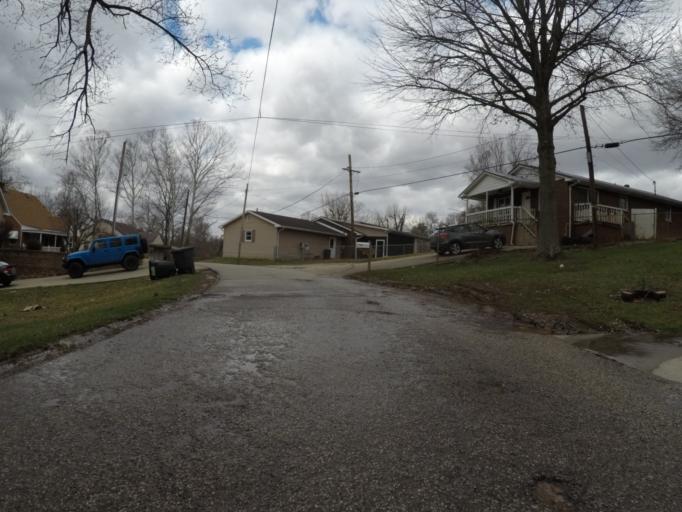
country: US
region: West Virginia
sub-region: Cabell County
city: Pea Ridge
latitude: 38.4054
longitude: -82.3795
